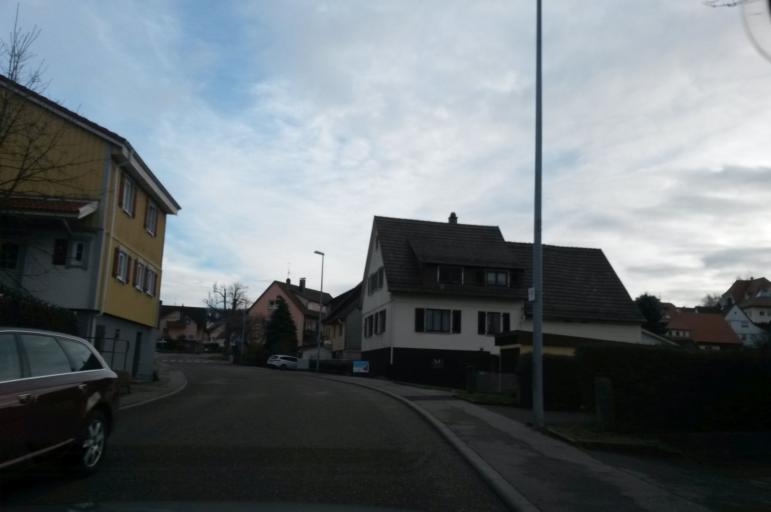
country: DE
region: Baden-Wuerttemberg
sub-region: Karlsruhe Region
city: Engelsbrand
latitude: 48.8318
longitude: 8.6435
